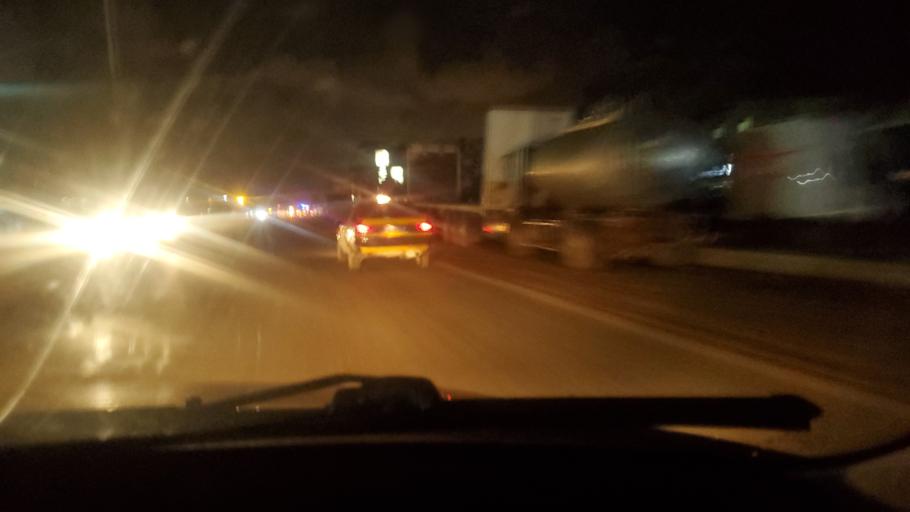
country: SN
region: Dakar
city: Pikine
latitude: 14.7436
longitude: -17.3879
